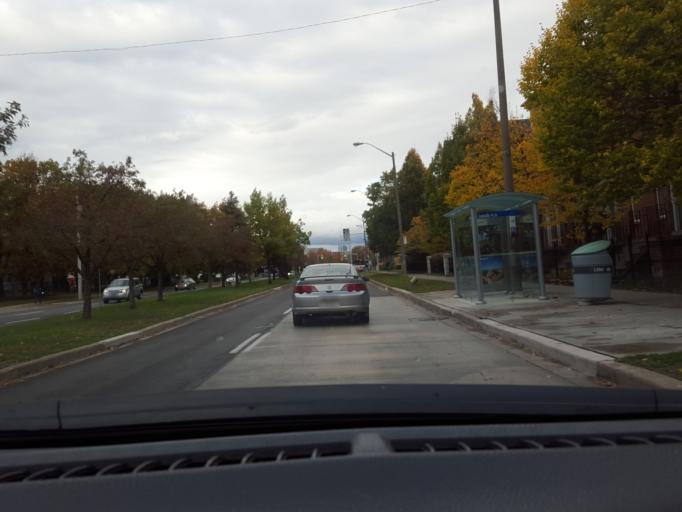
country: CA
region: Ontario
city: Toronto
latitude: 43.7035
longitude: -79.3512
